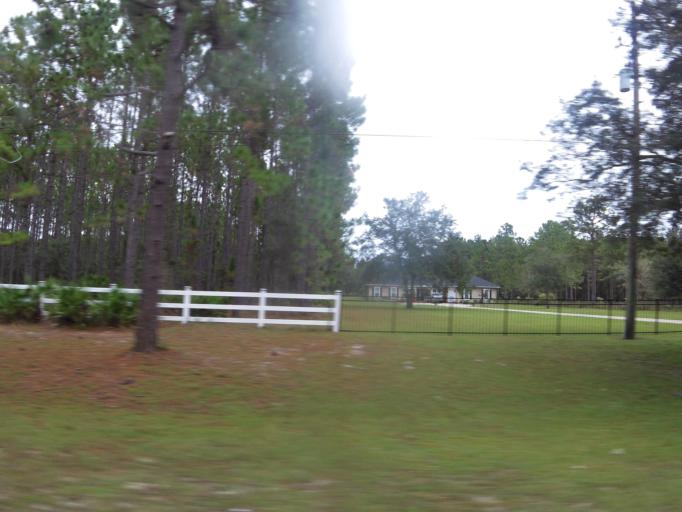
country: US
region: Florida
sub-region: Clay County
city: Lakeside
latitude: 30.2027
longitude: -81.8626
